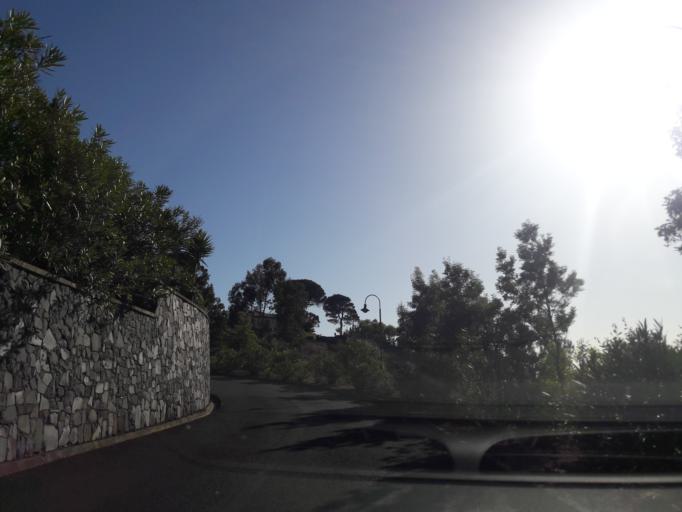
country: PT
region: Madeira
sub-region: Funchal
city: Nossa Senhora do Monte
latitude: 32.6549
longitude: -16.8719
